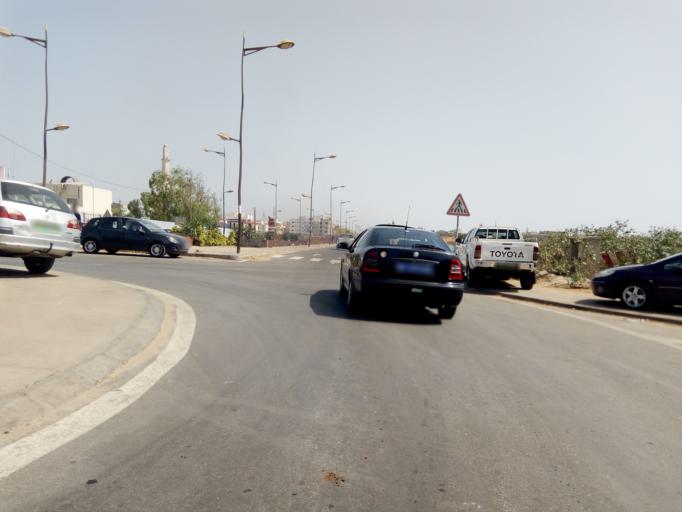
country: SN
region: Dakar
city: Dakar
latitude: 14.6997
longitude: -17.4501
